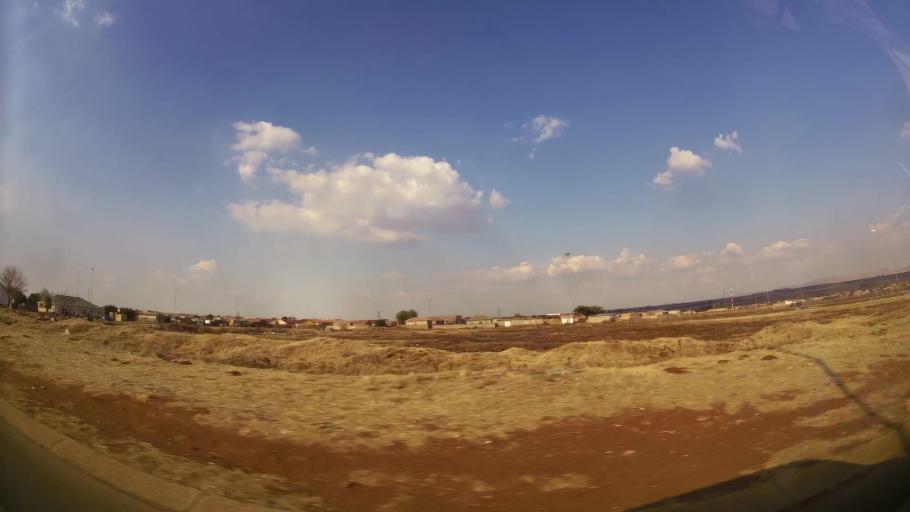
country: ZA
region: Gauteng
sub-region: Ekurhuleni Metropolitan Municipality
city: Germiston
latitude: -26.3662
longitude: 28.2194
